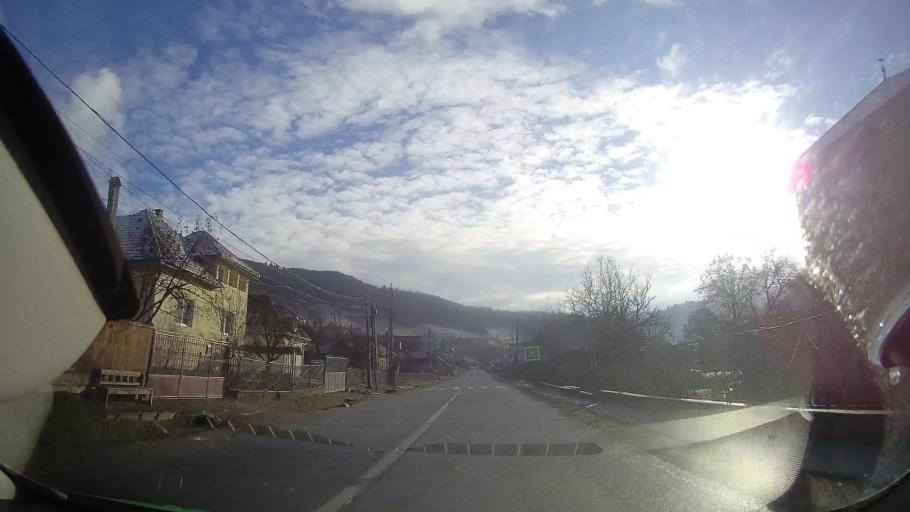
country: RO
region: Alba
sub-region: Comuna Sohodol
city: Sohodol
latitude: 46.3714
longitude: 23.0224
